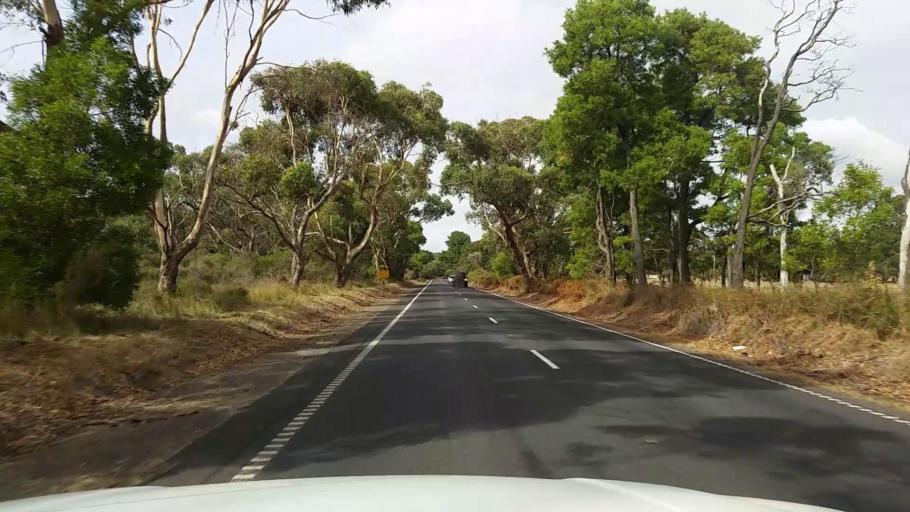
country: AU
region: Victoria
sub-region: Mornington Peninsula
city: Merricks
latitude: -38.3139
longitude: 145.0867
